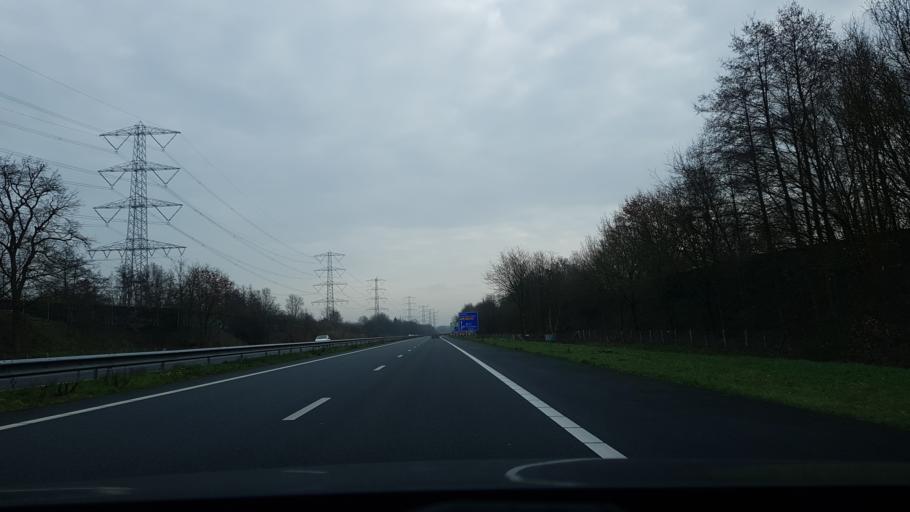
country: NL
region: Overijssel
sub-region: Gemeente Enschede
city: Enschede
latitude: 52.2014
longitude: 6.8683
